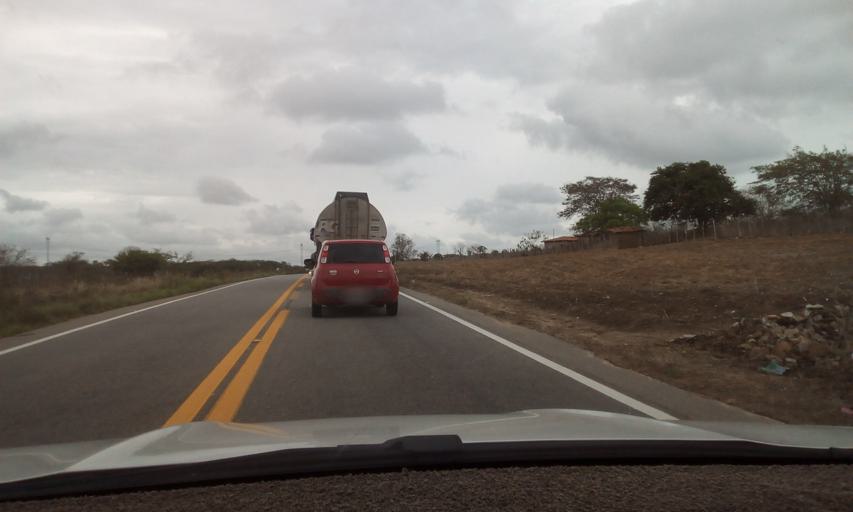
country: BR
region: Paraiba
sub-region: Areia
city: Remigio
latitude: -6.9324
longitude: -35.8334
